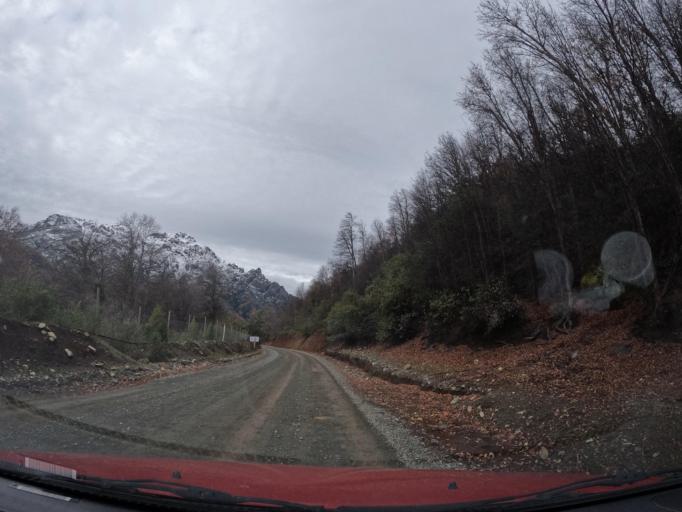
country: CL
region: Maule
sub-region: Provincia de Linares
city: Colbun
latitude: -35.8589
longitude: -71.1494
